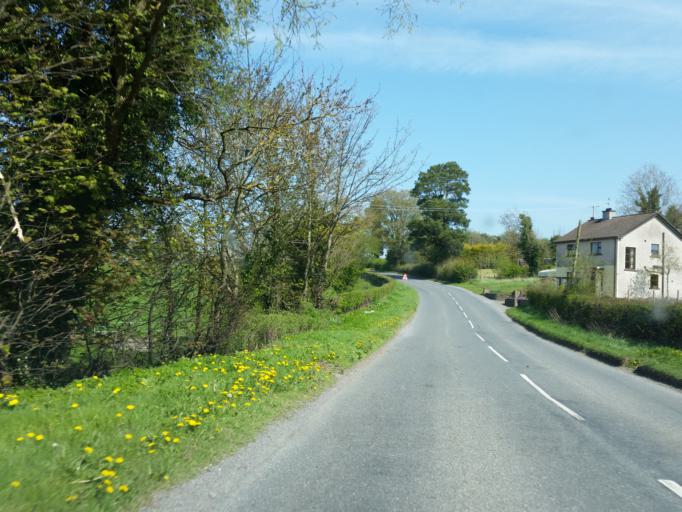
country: GB
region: Northern Ireland
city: Lisnaskea
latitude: 54.2650
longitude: -7.4470
